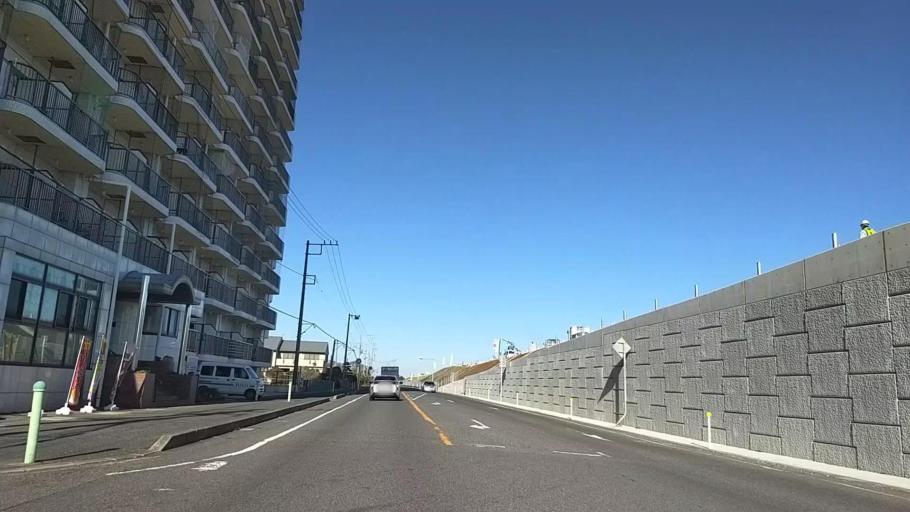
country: JP
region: Chiba
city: Togane
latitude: 35.4530
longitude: 140.4039
